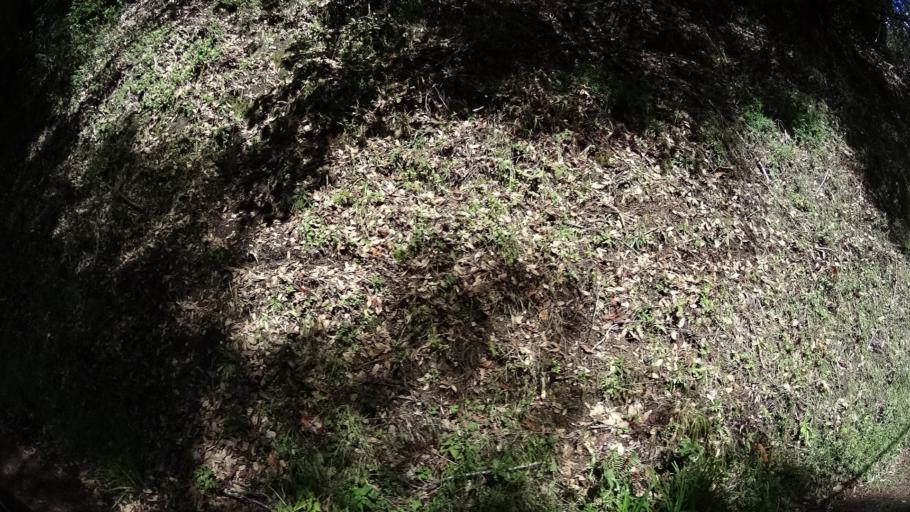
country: US
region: California
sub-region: Humboldt County
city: Blue Lake
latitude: 40.7614
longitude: -123.9541
